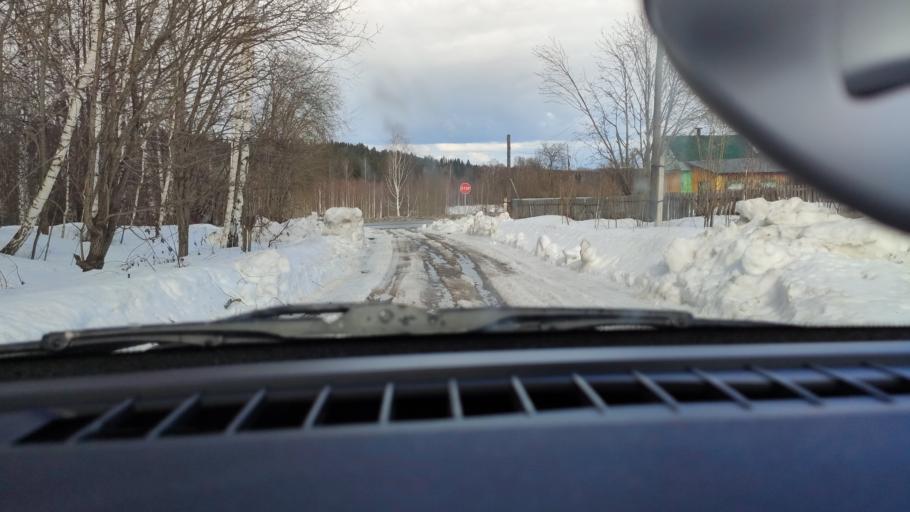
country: RU
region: Perm
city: Nytva
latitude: 57.9264
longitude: 55.4357
